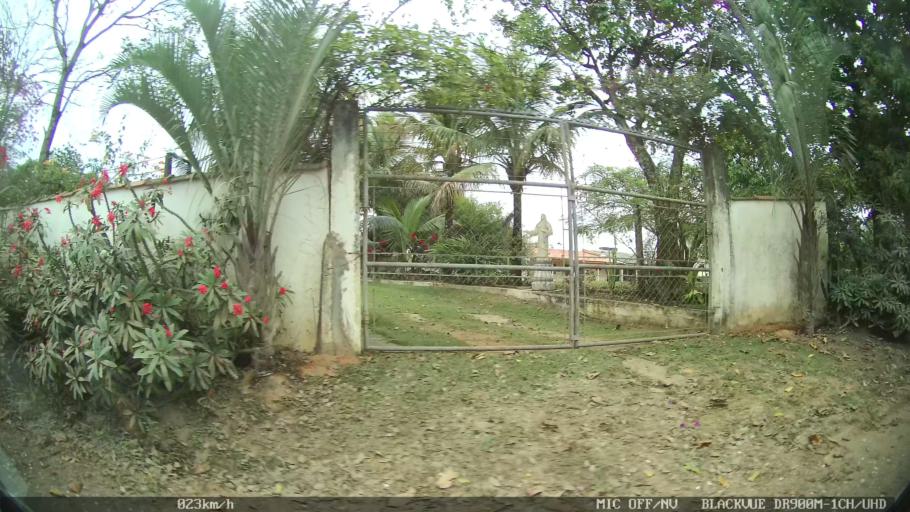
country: BR
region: Sao Paulo
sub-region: Americana
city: Americana
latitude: -22.6648
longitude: -47.3750
